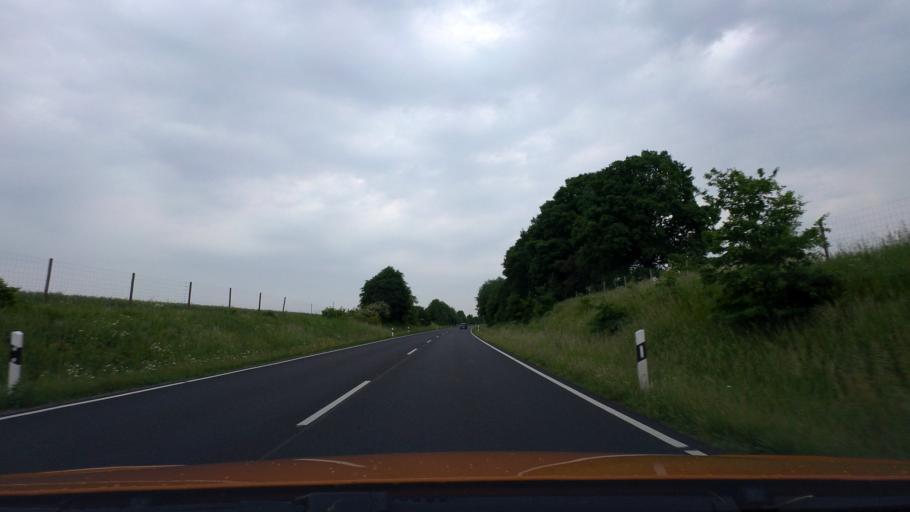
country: DE
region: Lower Saxony
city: Wietzen
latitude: 52.6654
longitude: 9.1030
